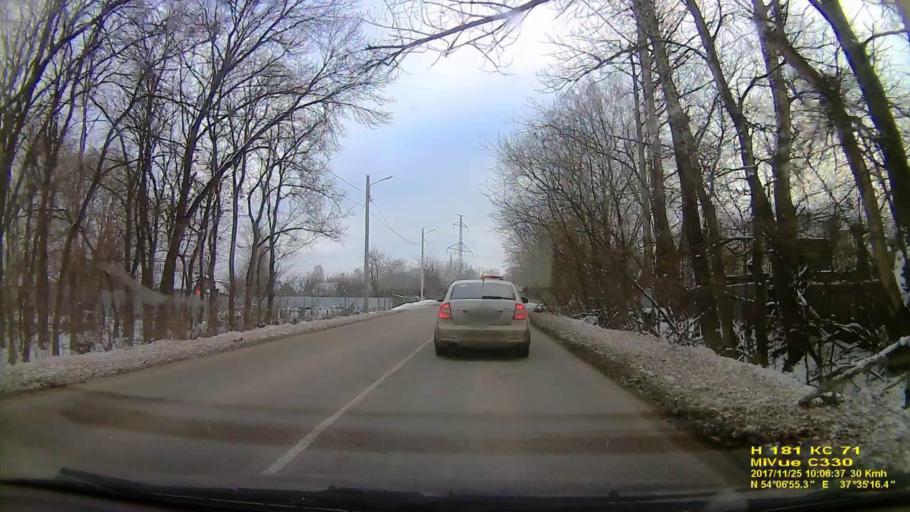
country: RU
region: Tula
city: Skuratovskiy
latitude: 54.1153
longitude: 37.5880
